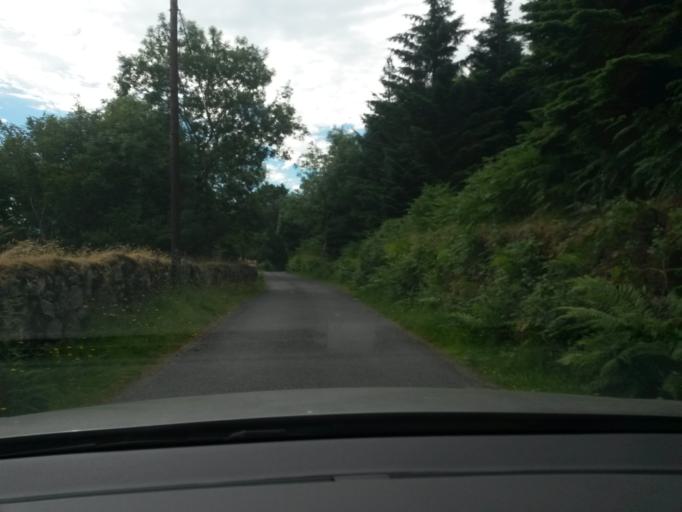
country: IE
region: Leinster
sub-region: Wicklow
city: Enniskerry
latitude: 53.1718
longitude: -6.2417
